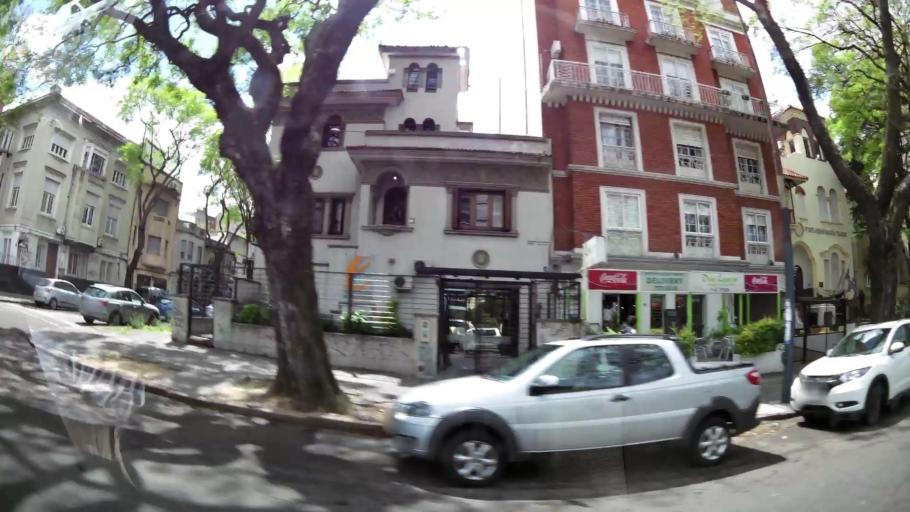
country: UY
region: Montevideo
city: Montevideo
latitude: -34.9077
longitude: -56.1634
